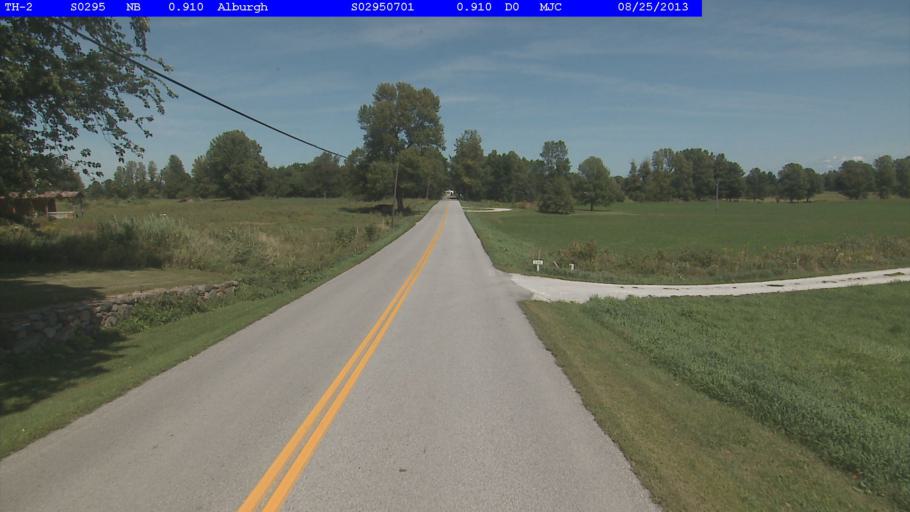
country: US
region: Vermont
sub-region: Franklin County
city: Swanton
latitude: 44.9869
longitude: -73.2255
